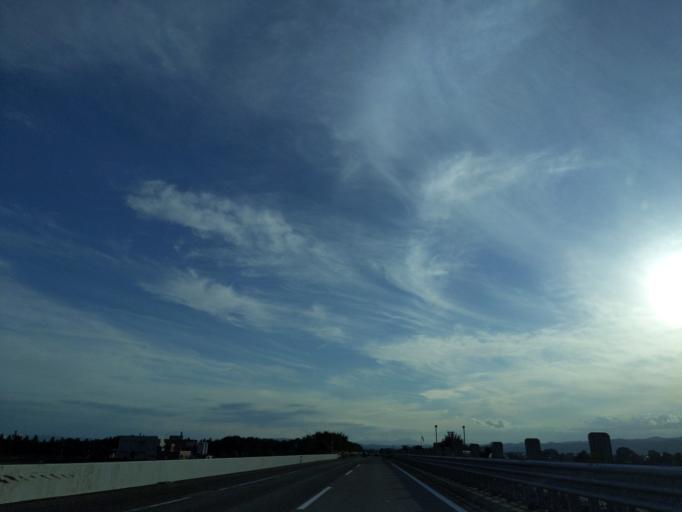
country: JP
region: Niigata
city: Nagaoka
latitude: 37.5030
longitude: 138.8422
